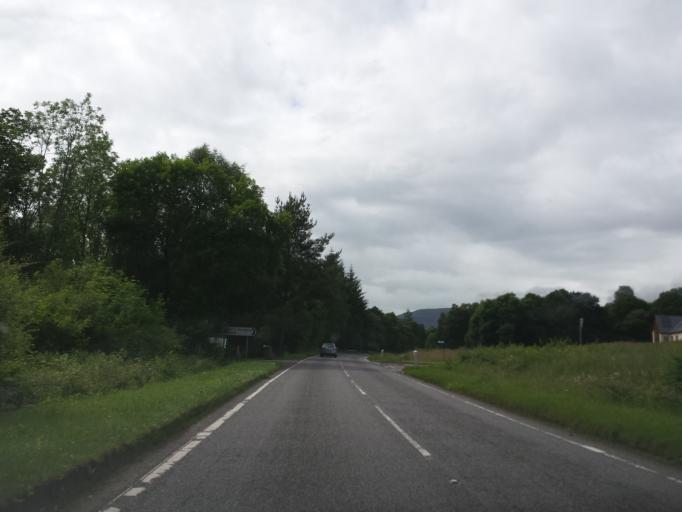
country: GB
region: Scotland
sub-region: Highland
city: Fort William
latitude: 56.8536
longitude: -5.1837
